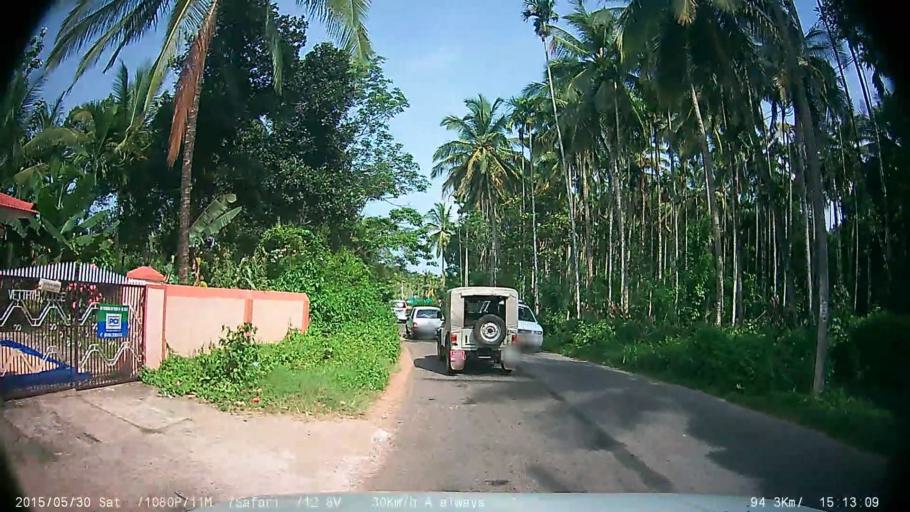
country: IN
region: Kerala
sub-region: Wayanad
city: Panamaram
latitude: 11.7924
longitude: 76.0417
